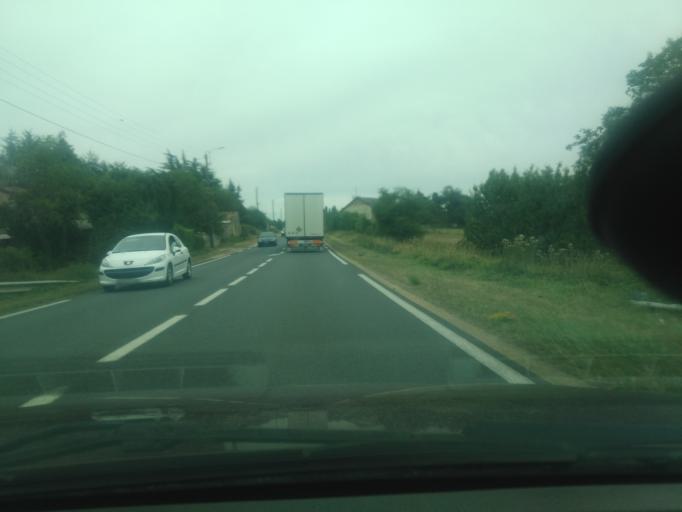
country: FR
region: Poitou-Charentes
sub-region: Departement de la Vienne
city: Sevres-Anxaumont
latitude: 46.5598
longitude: 0.4515
